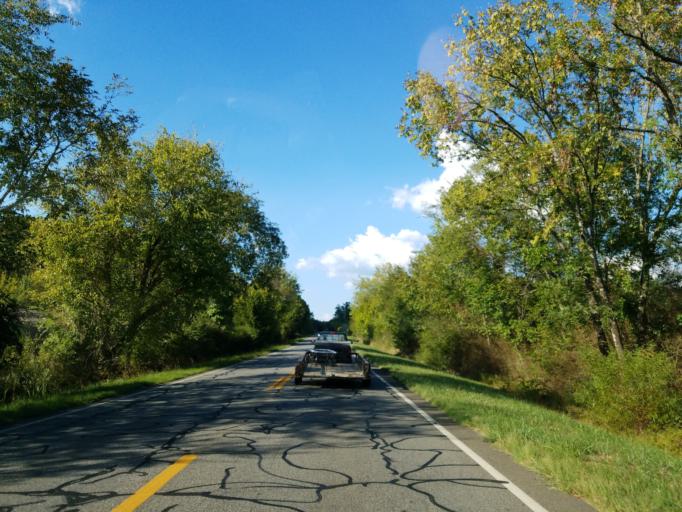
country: US
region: Georgia
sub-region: Murray County
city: Chatsworth
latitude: 34.5612
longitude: -84.7079
